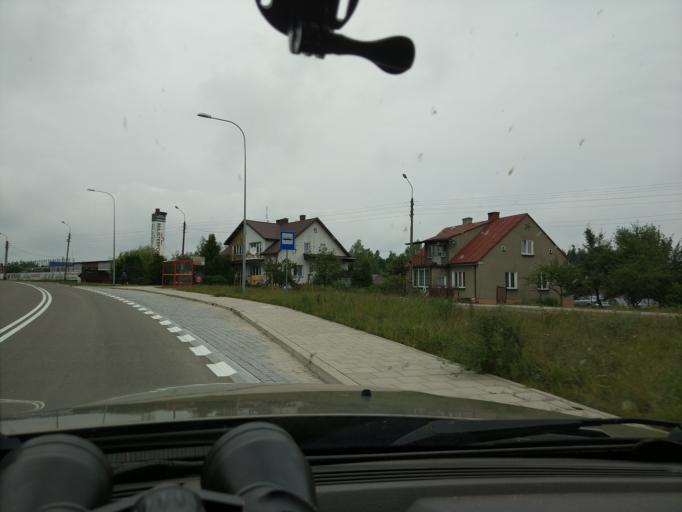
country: PL
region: Podlasie
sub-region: Powiat zambrowski
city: Szumowo
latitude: 52.9151
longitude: 22.0914
